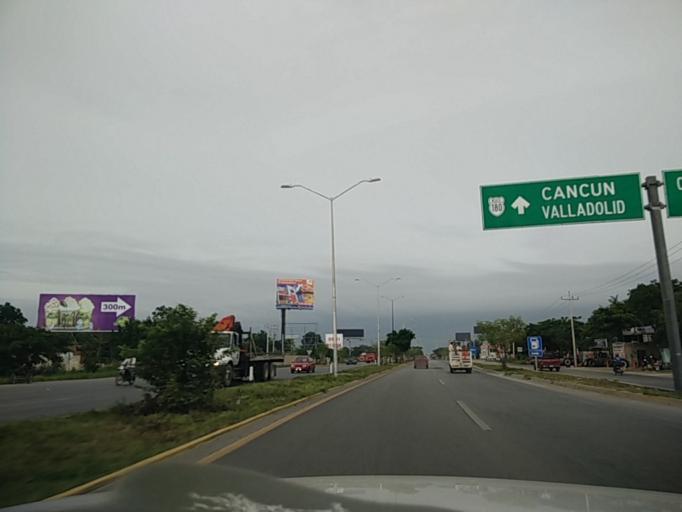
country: MX
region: Yucatan
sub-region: Kanasin
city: Kanasin
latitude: 20.9550
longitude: -89.5661
